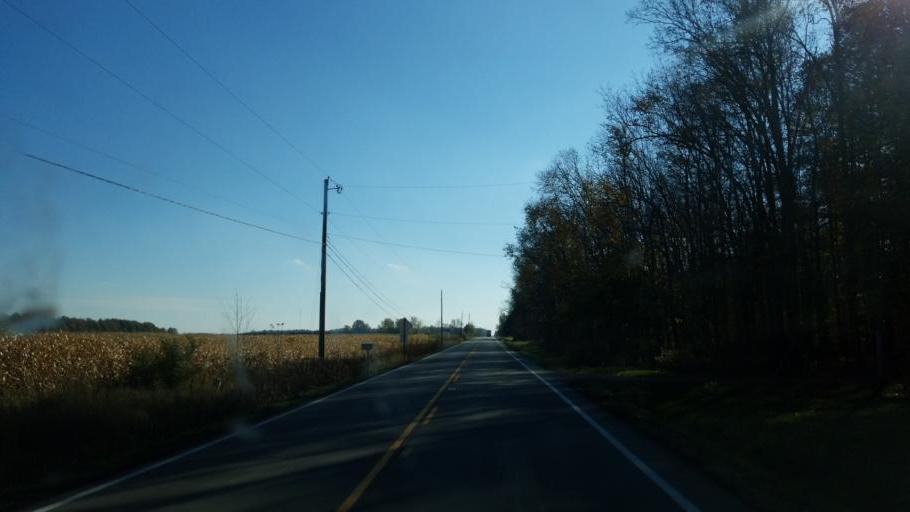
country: US
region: Ohio
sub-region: Wayne County
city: West Salem
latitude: 40.9798
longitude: -82.2153
